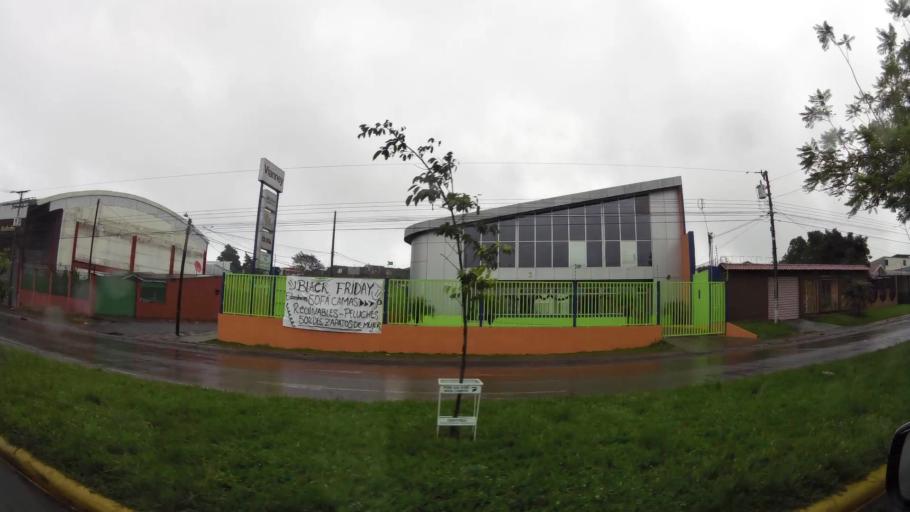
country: CR
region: Cartago
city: Cartago
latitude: 9.8667
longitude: -83.9342
